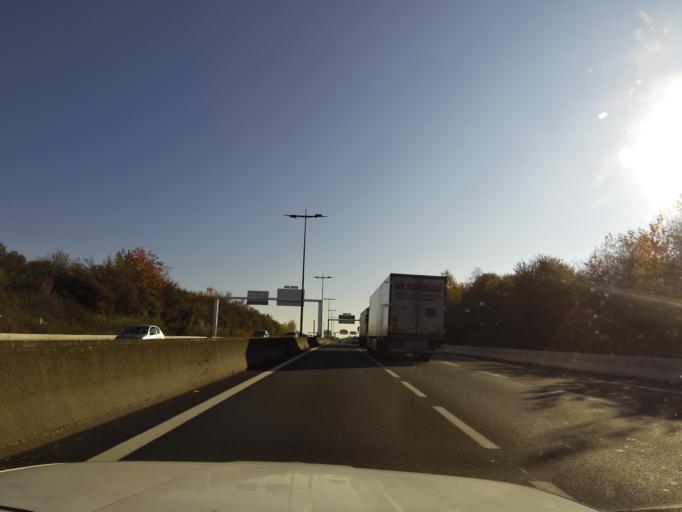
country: FR
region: Rhone-Alpes
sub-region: Departement du Rhone
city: Decines-Charpieu
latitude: 45.7570
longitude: 4.9854
